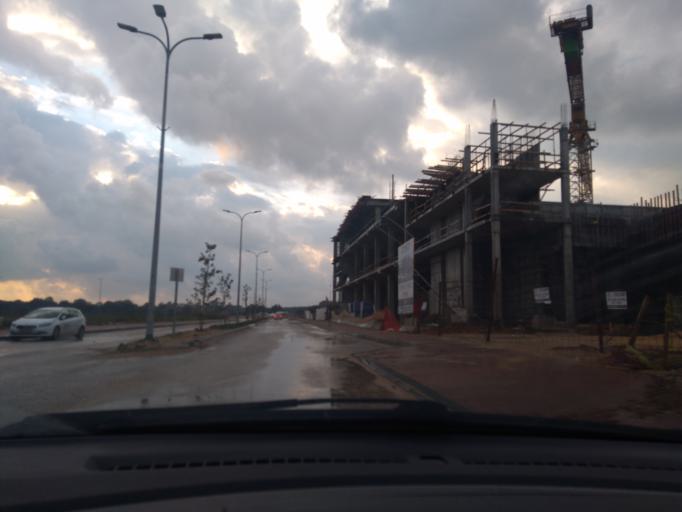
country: IL
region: Central District
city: Elyakhin
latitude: 32.4009
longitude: 34.8944
